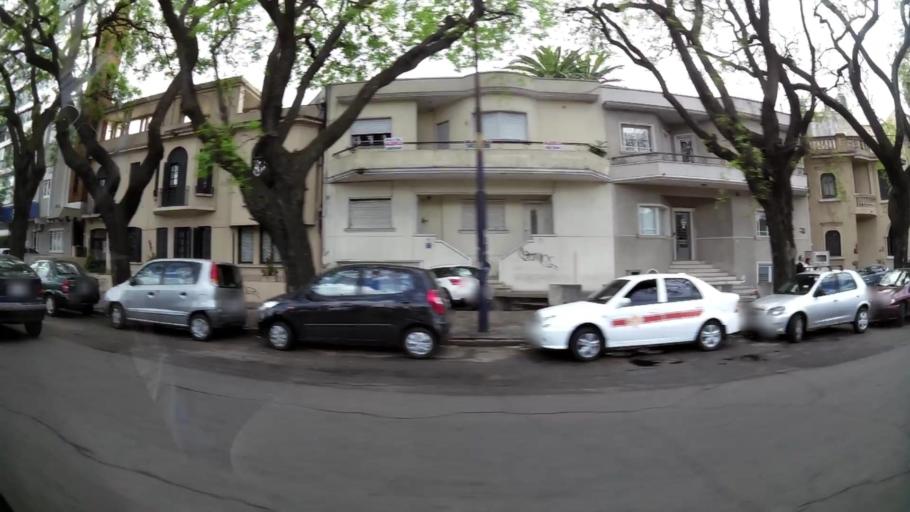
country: UY
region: Montevideo
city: Montevideo
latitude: -34.9124
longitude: -56.1630
